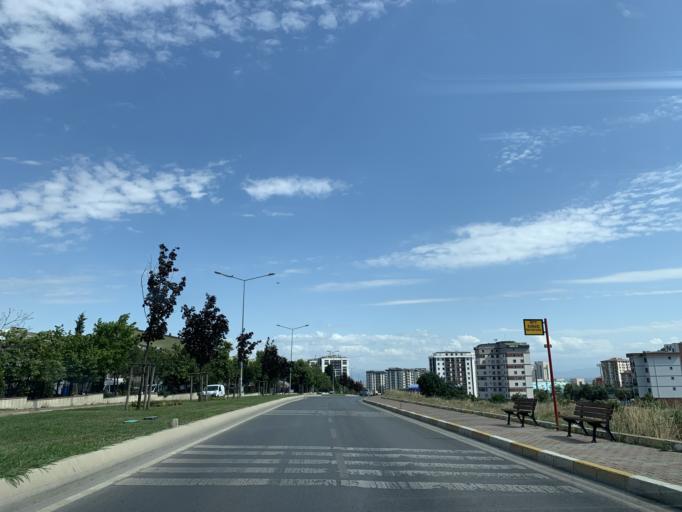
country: TR
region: Istanbul
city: Pendik
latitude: 40.8957
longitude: 29.2608
